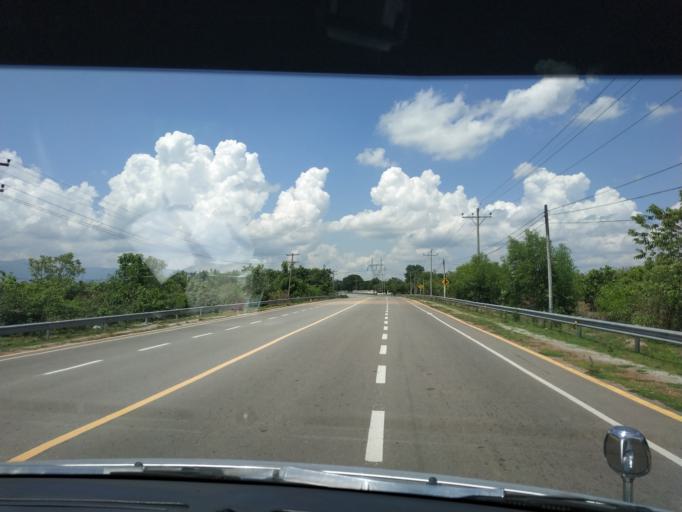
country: MM
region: Mon
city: Kyaikto
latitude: 17.3320
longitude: 97.0347
